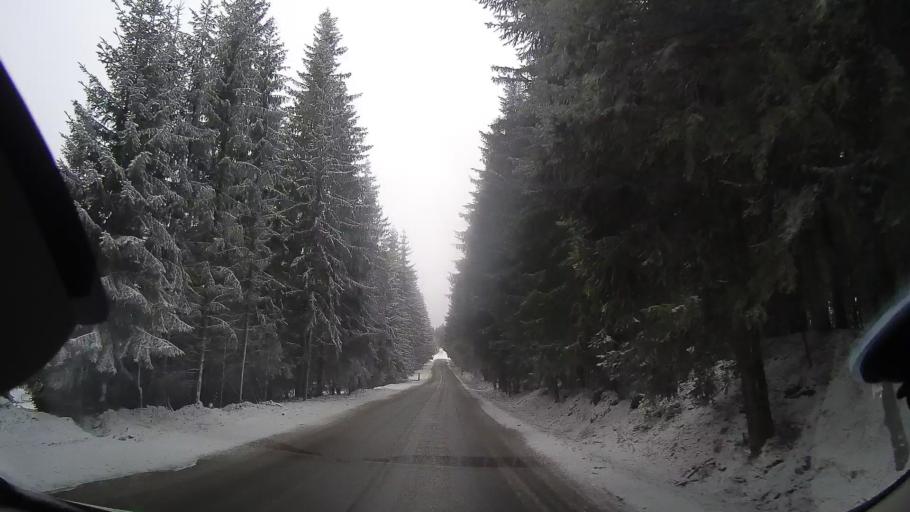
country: RO
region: Cluj
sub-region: Comuna Belis
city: Belis
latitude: 46.6383
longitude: 23.0480
